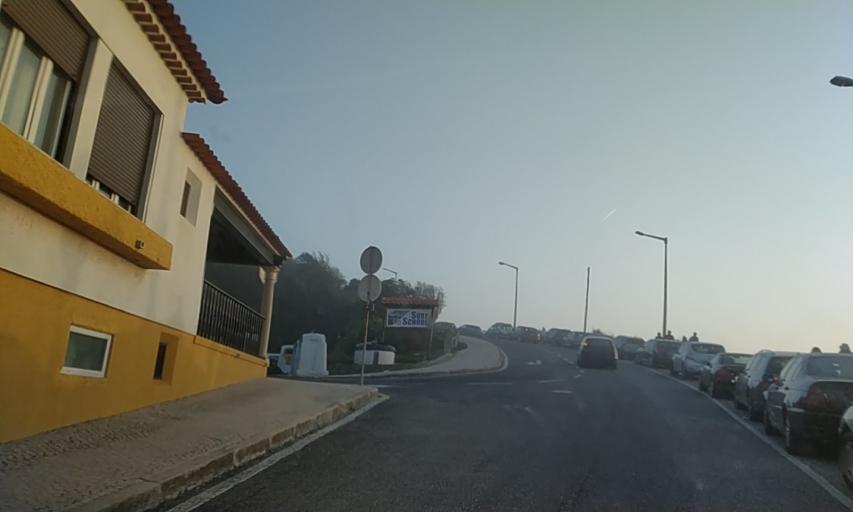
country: PT
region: Leiria
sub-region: Alcobaca
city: Pataias
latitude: 39.7554
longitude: -9.0320
